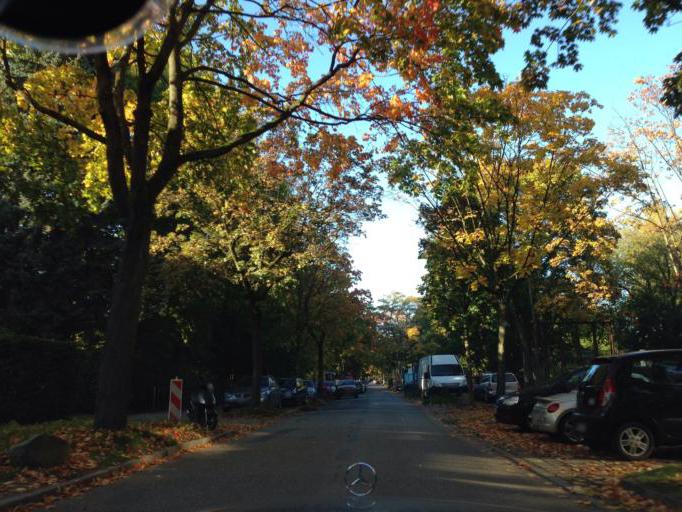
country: DE
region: Hamburg
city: Wandsbek
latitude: 53.5672
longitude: 10.1004
